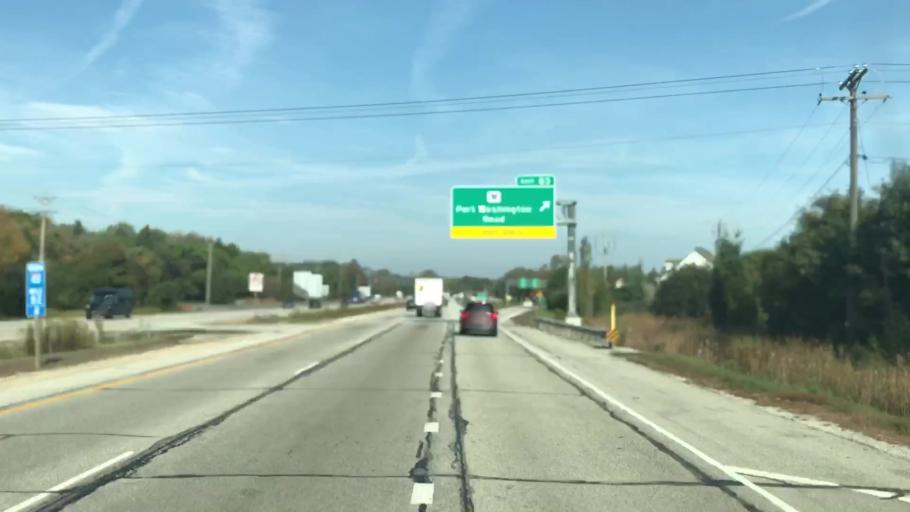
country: US
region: Wisconsin
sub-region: Milwaukee County
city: River Hills
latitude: 43.1838
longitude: -87.9206
